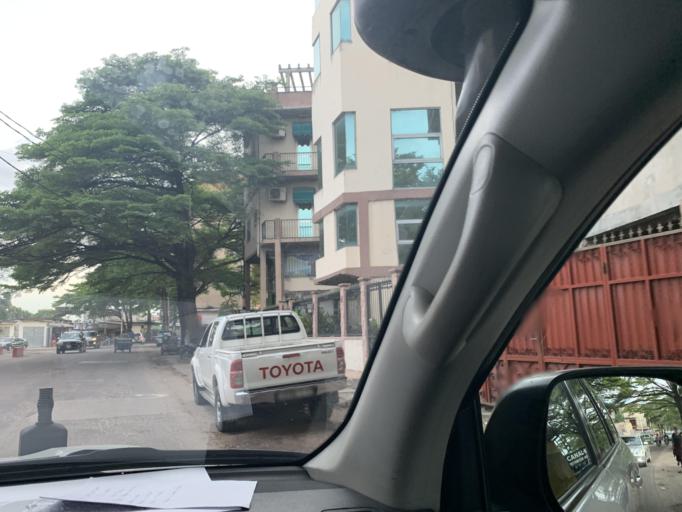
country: CG
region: Brazzaville
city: Brazzaville
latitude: -4.2622
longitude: 15.2895
